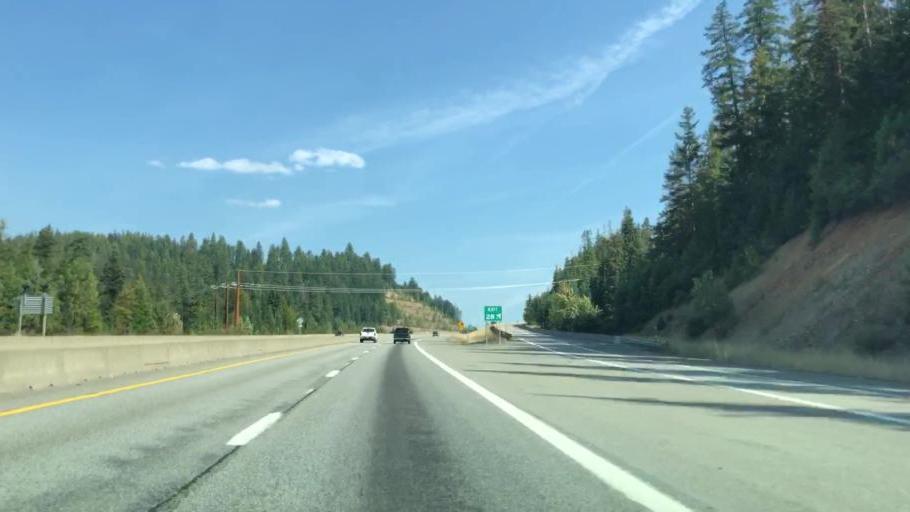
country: US
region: Idaho
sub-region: Kootenai County
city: Coeur d'Alene
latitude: 47.6239
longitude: -116.5336
